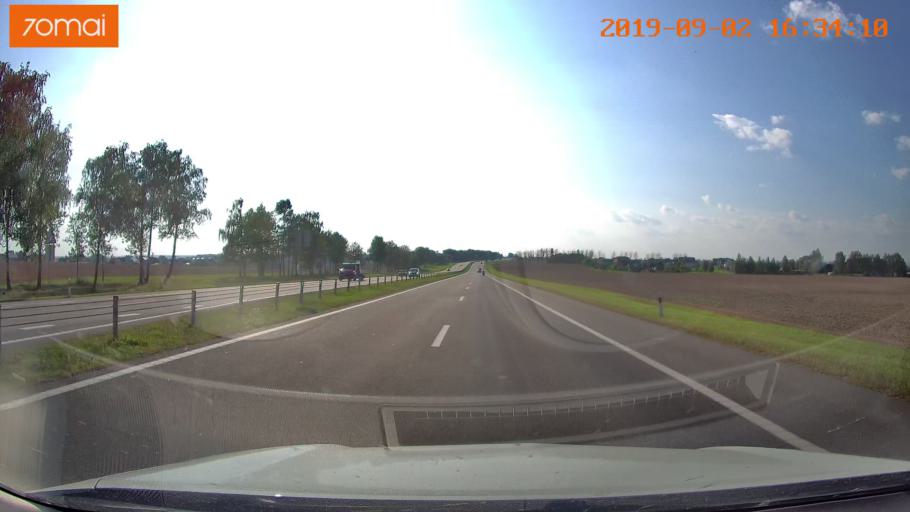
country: BY
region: Minsk
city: Smilavichy
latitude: 53.7596
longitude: 28.0451
